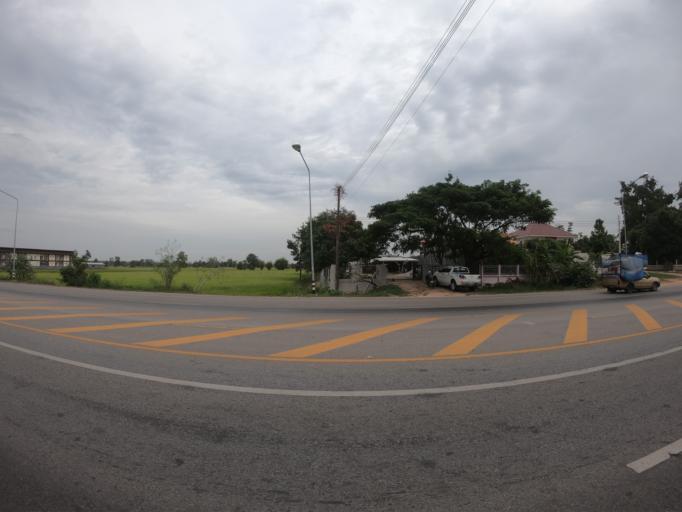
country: TH
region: Roi Et
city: Chiang Khwan
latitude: 16.1343
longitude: 103.8530
